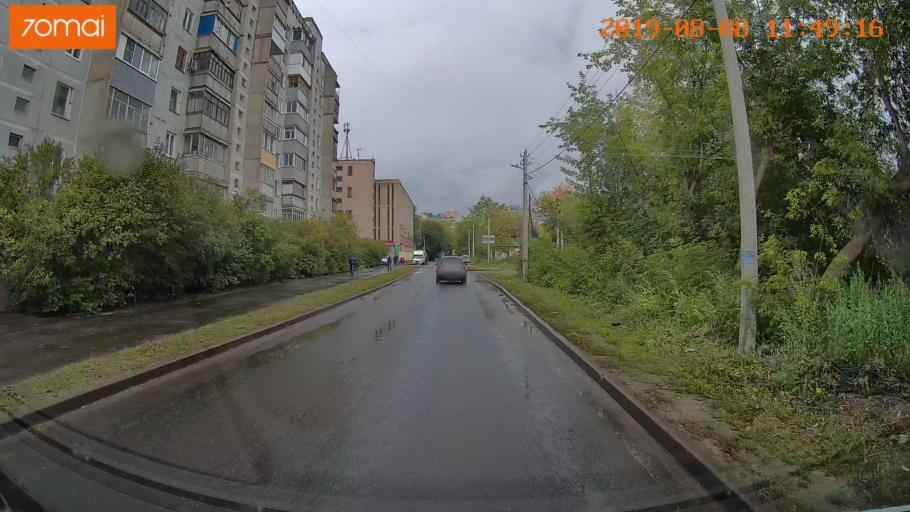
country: RU
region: Ivanovo
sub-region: Gorod Ivanovo
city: Ivanovo
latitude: 56.9769
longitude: 40.9819
